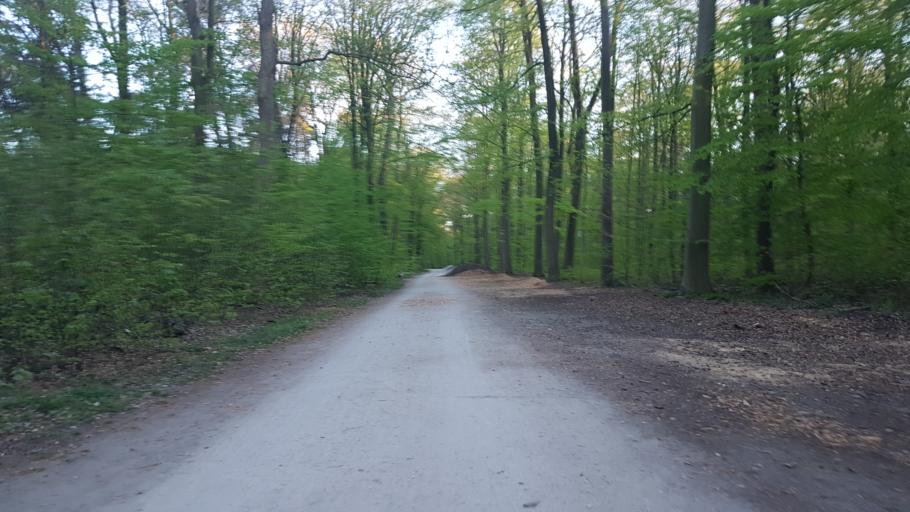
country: DE
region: Lower Saxony
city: Hannover
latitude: 52.3869
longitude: 9.7819
